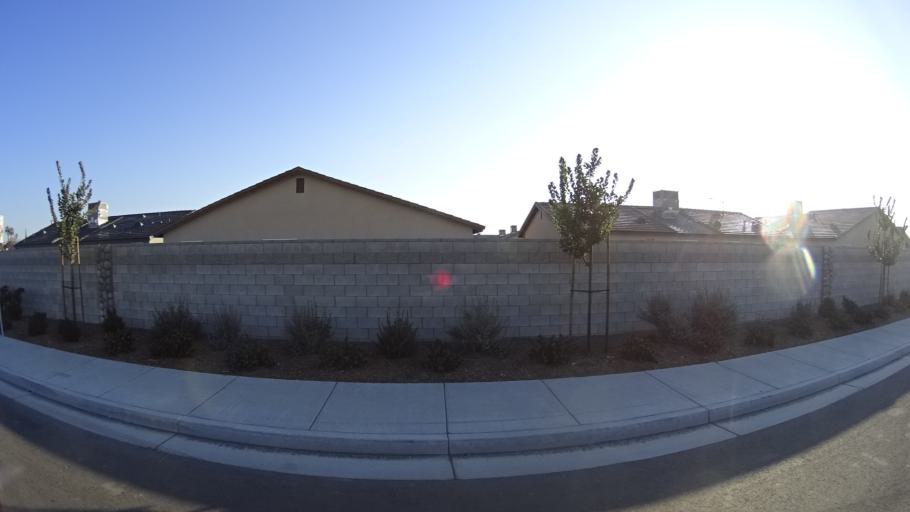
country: US
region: California
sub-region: Kern County
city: Greenfield
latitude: 35.2984
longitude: -118.9942
